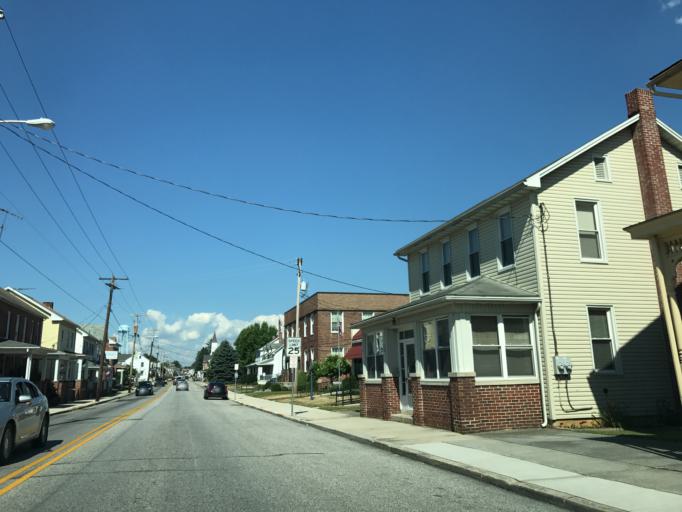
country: US
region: Pennsylvania
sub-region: Adams County
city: McSherrystown
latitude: 39.8037
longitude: -77.0197
